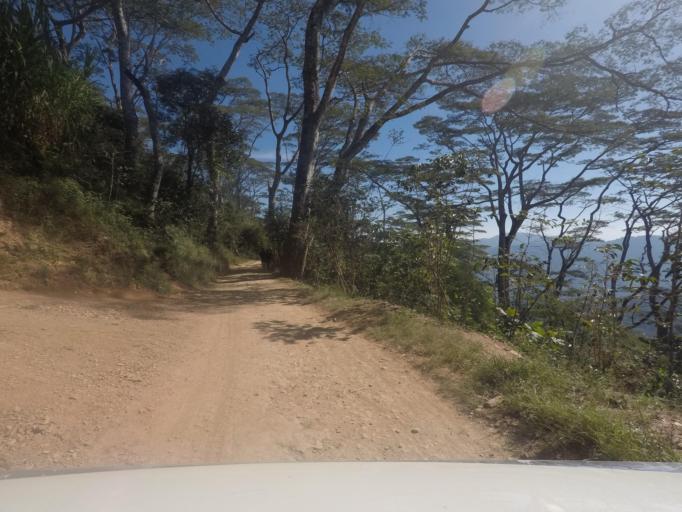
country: TL
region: Ermera
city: Gleno
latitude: -8.7397
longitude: 125.3466
